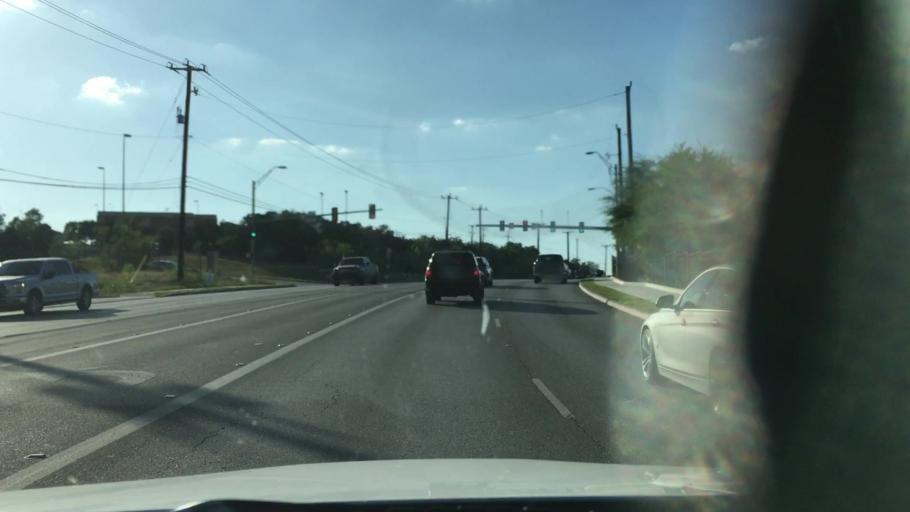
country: US
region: Texas
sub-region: Bexar County
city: Timberwood Park
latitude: 29.6559
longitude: -98.4314
